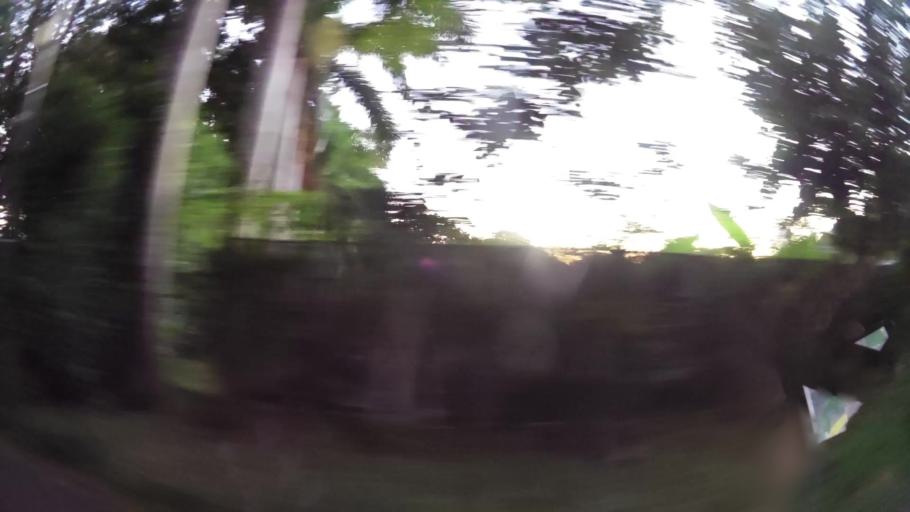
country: MU
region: Moka
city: Moka
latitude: -20.2229
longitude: 57.5010
